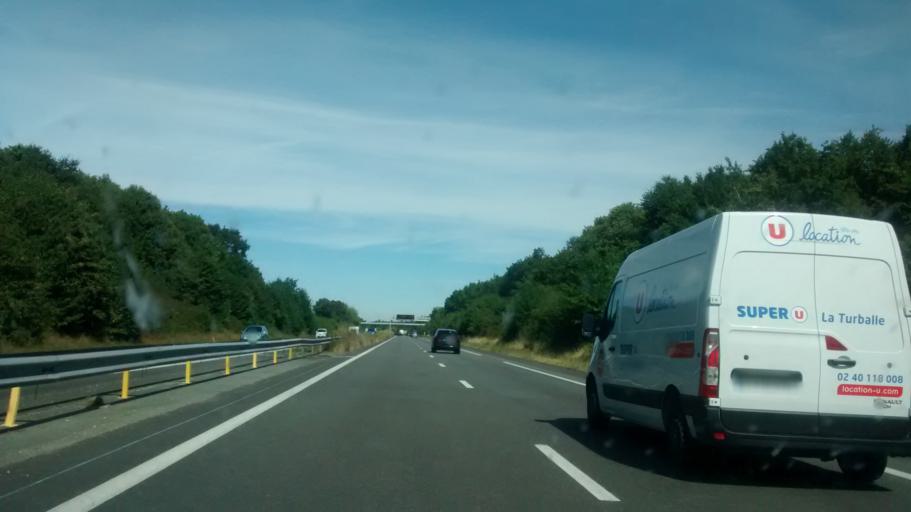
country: FR
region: Poitou-Charentes
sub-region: Departement de la Charente-Maritime
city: Pons
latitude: 45.5500
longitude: -0.6041
